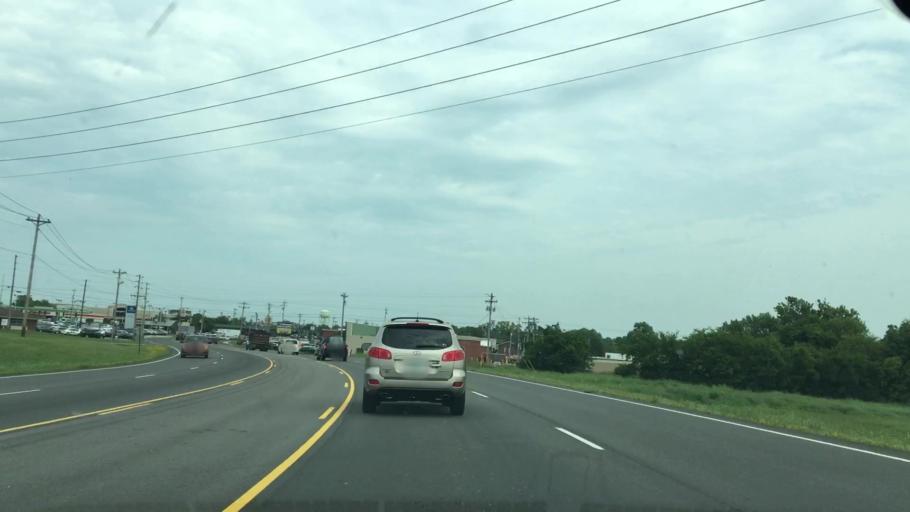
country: US
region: Tennessee
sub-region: Wilson County
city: Lebanon
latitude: 36.2103
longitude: -86.3217
